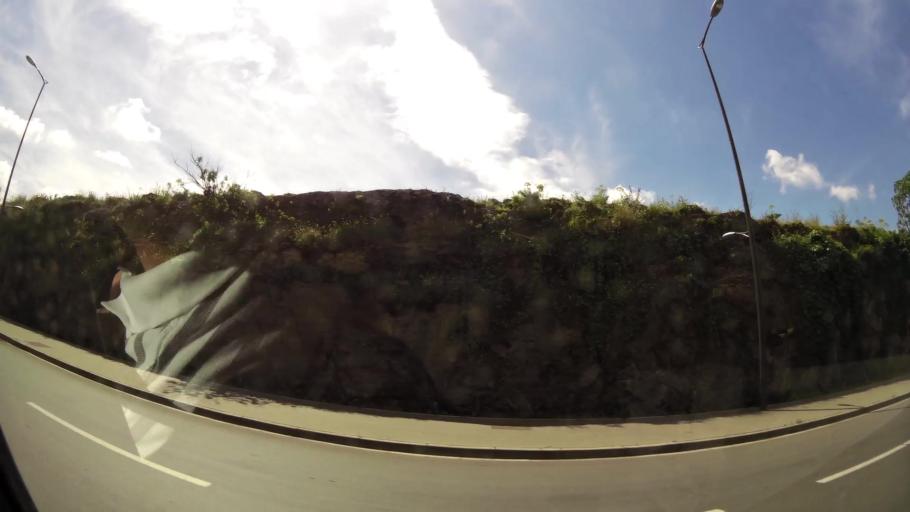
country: MA
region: Grand Casablanca
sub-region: Casablanca
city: Casablanca
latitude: 33.6021
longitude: -7.5549
